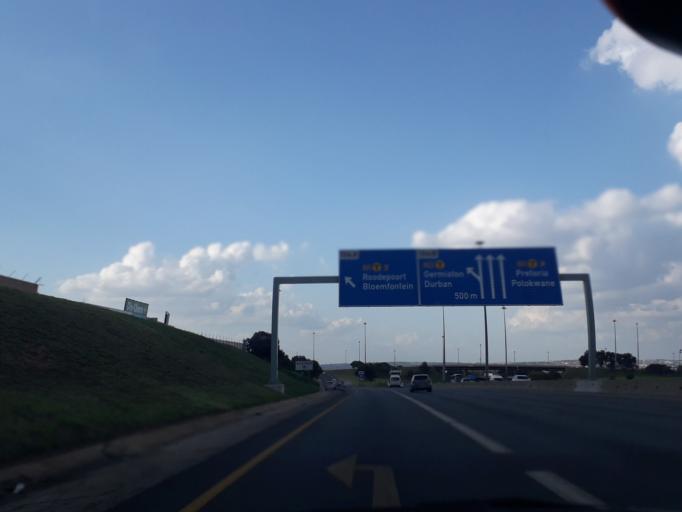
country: ZA
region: Gauteng
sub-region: City of Johannesburg Metropolitan Municipality
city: Midrand
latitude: -26.0532
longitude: 28.0938
